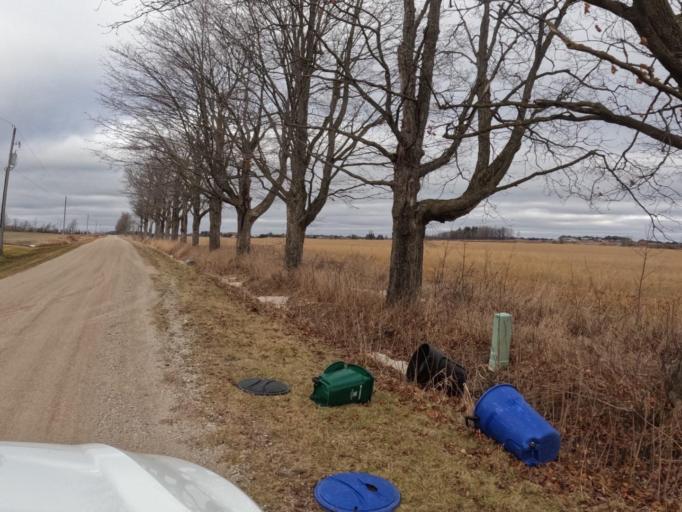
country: CA
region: Ontario
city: Shelburne
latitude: 43.8880
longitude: -80.3284
